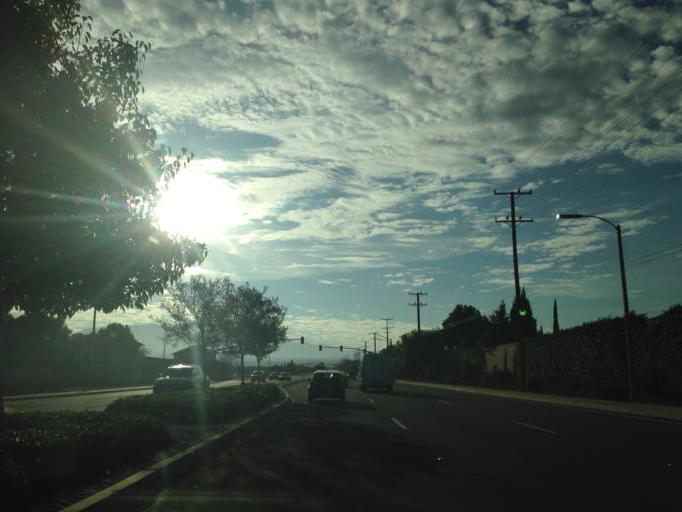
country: US
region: California
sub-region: Riverside County
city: Temecula
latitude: 33.4696
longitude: -117.1211
